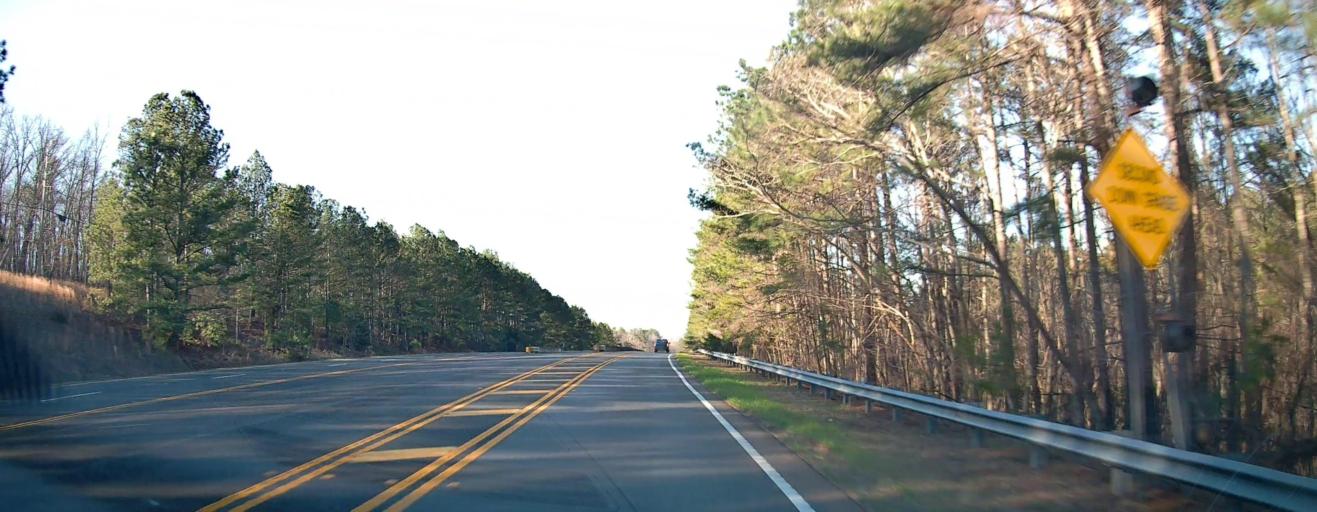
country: US
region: Georgia
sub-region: Meriwether County
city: Manchester
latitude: 32.8802
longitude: -84.6802
